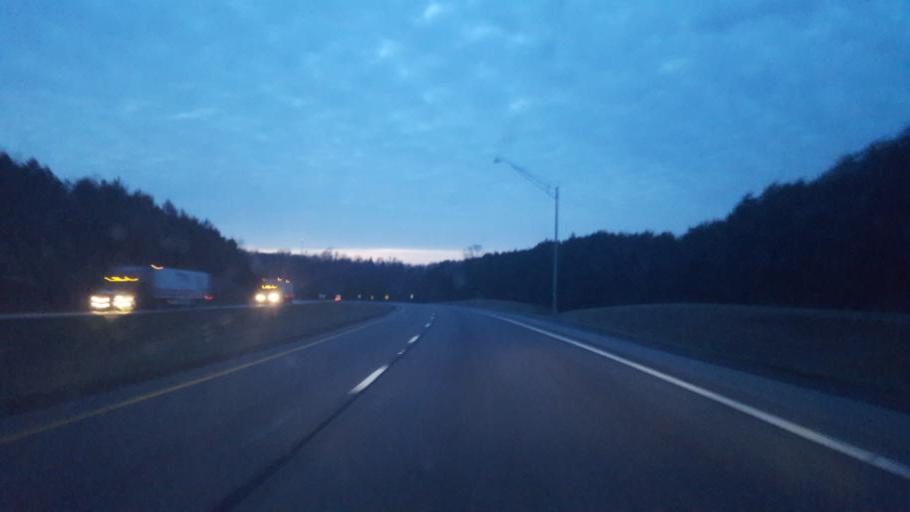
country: US
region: Ohio
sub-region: Jackson County
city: Jackson
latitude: 39.0672
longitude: -82.6266
